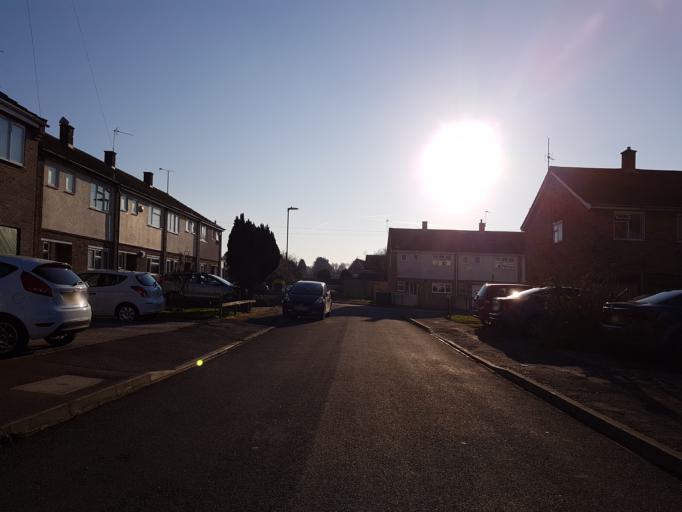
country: GB
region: England
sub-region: Cambridgeshire
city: Fulbourn
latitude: 52.1897
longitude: 0.1724
